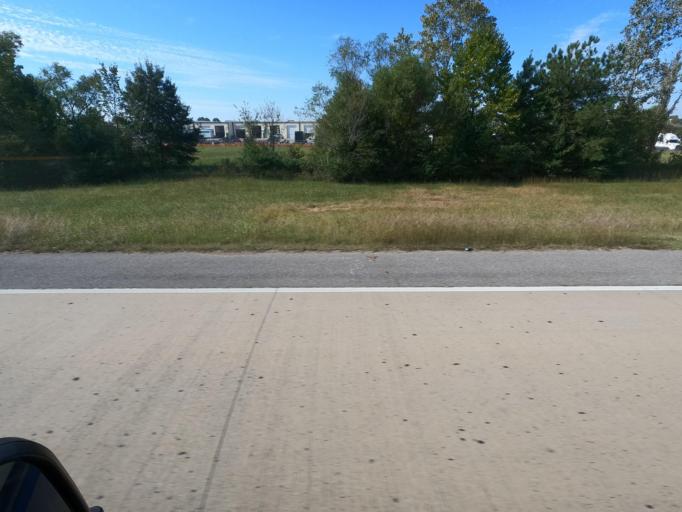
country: US
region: Tennessee
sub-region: Shelby County
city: Arlington
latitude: 35.2843
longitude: -89.6822
